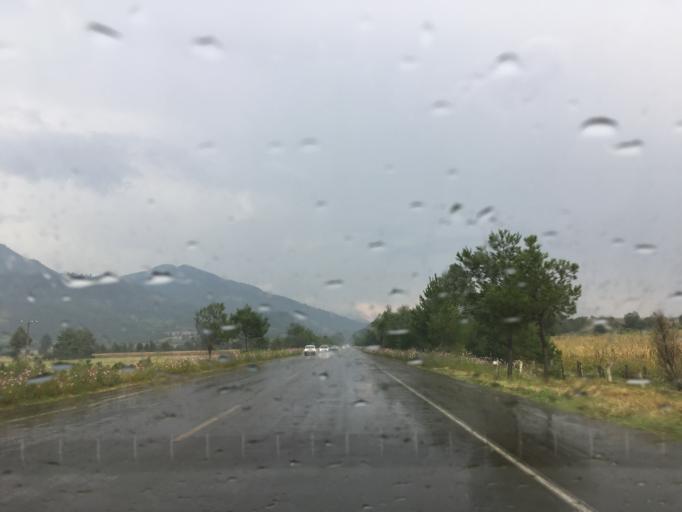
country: MX
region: Michoacan
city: Angahuan
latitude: 19.5663
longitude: -102.2433
